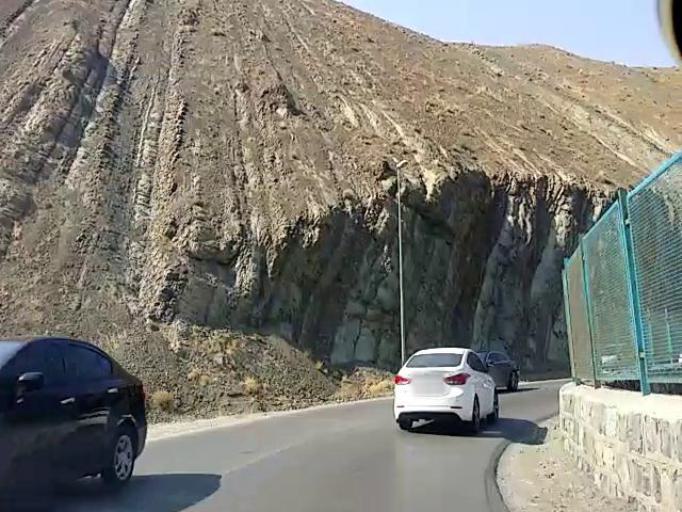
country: IR
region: Alborz
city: Karaj
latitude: 35.9711
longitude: 51.0935
